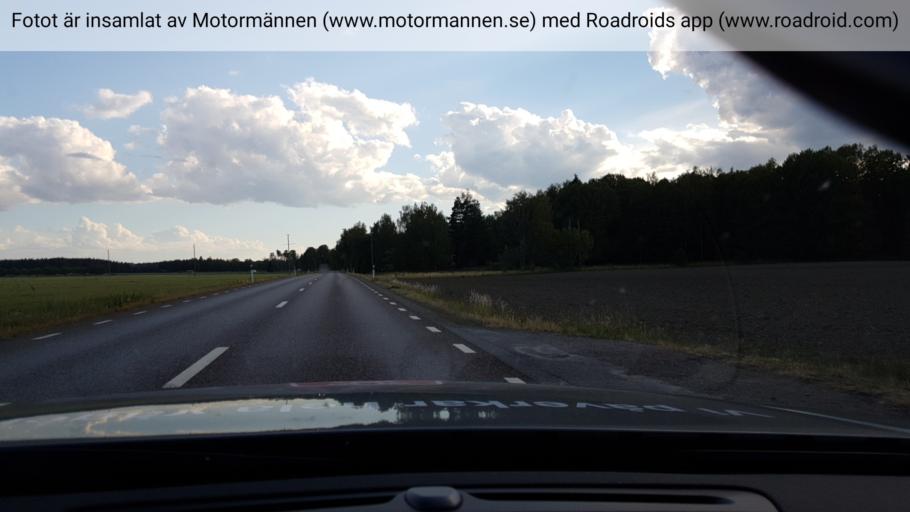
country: SE
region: Uppsala
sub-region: Enkopings Kommun
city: Irsta
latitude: 59.8061
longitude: 16.9114
